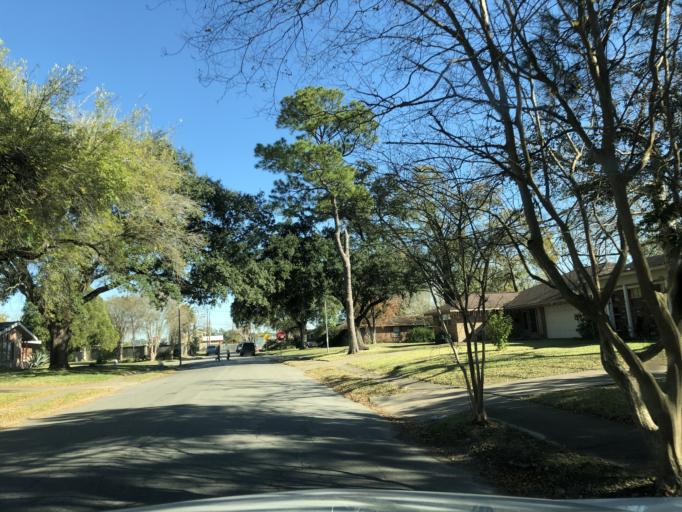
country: US
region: Texas
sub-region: Harris County
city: Bellaire
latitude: 29.6931
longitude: -95.5018
